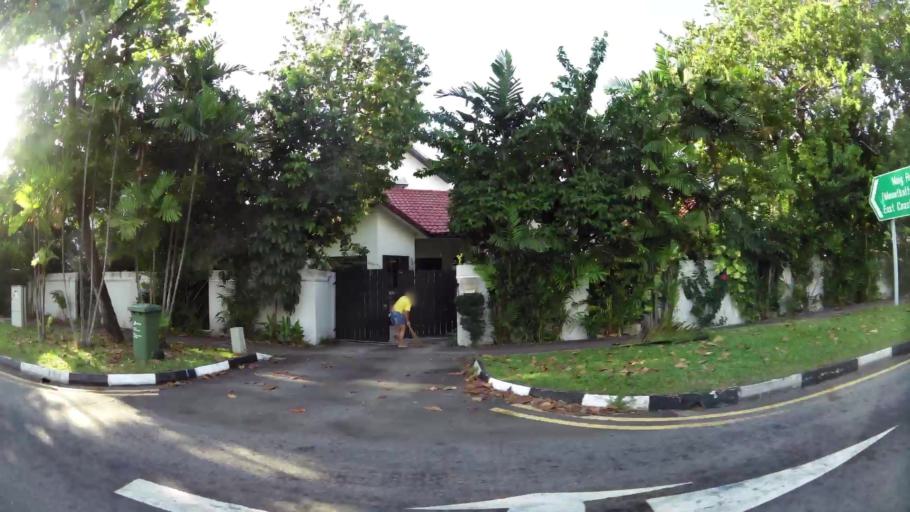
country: SG
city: Singapore
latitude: 1.3094
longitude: 103.8980
